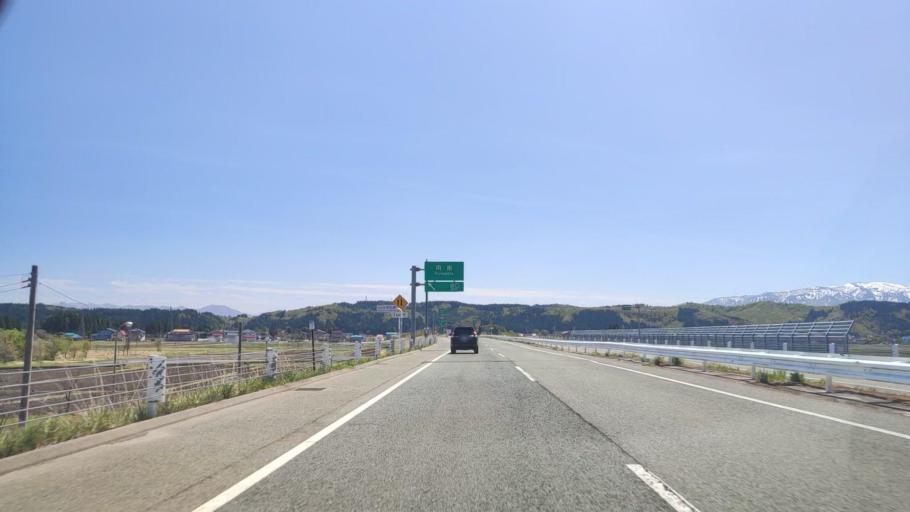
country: JP
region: Yamagata
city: Shinjo
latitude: 38.7074
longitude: 140.3088
